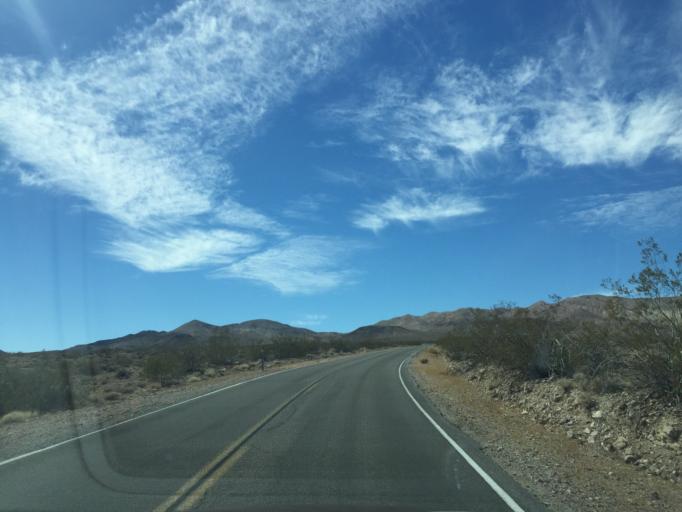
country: US
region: Nevada
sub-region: Nye County
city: Beatty
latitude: 36.2557
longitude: -116.6731
